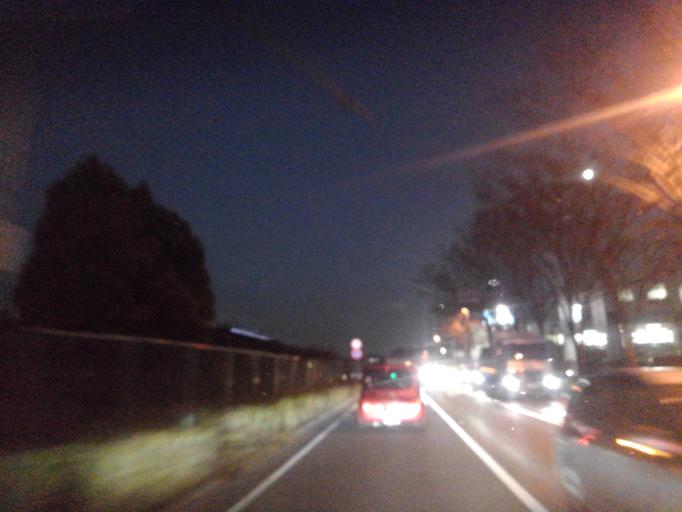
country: JP
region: Tokyo
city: Hino
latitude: 35.6191
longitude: 139.4547
